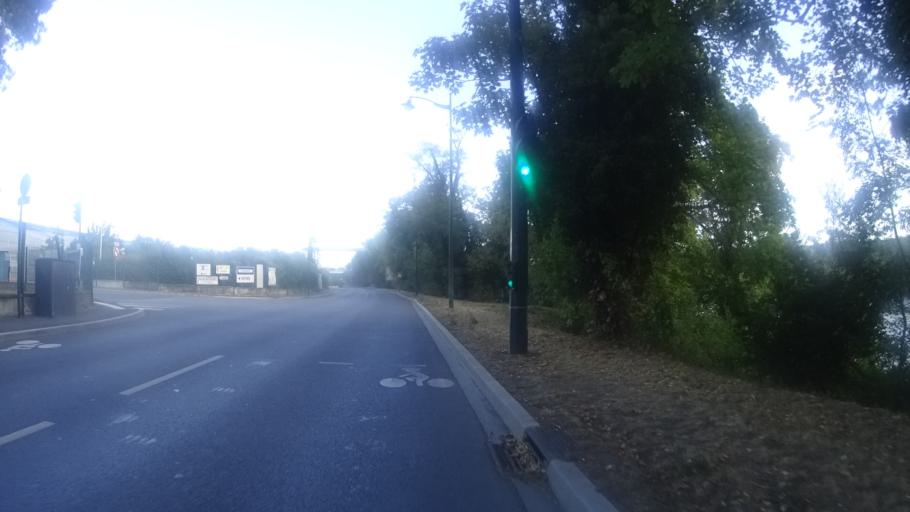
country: FR
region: Ile-de-France
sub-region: Departement de l'Essonne
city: Etiolles
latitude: 48.6222
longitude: 2.4730
